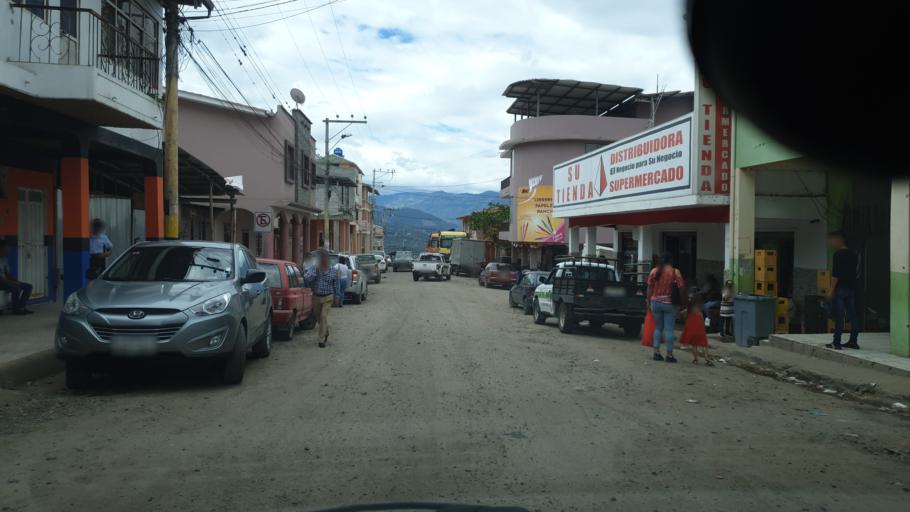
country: EC
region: Azuay
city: Cuenca
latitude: -3.2757
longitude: -79.3137
